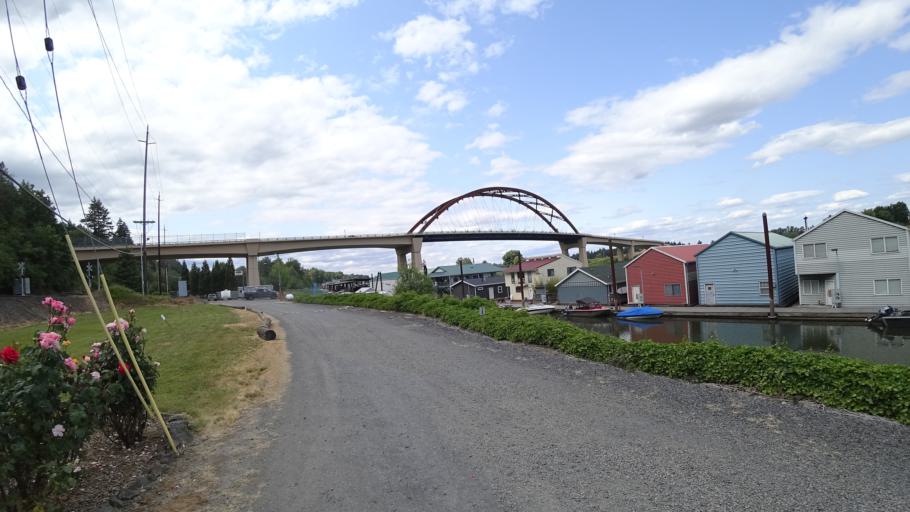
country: US
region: Oregon
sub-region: Washington County
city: Bethany
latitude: 45.6260
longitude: -122.8166
